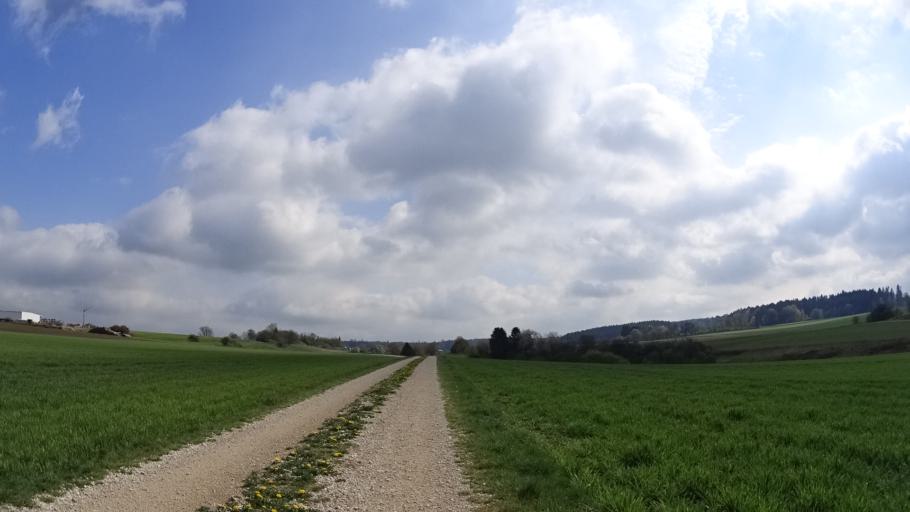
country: DE
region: Bavaria
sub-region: Upper Bavaria
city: Bohmfeld
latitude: 48.8811
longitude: 11.4061
